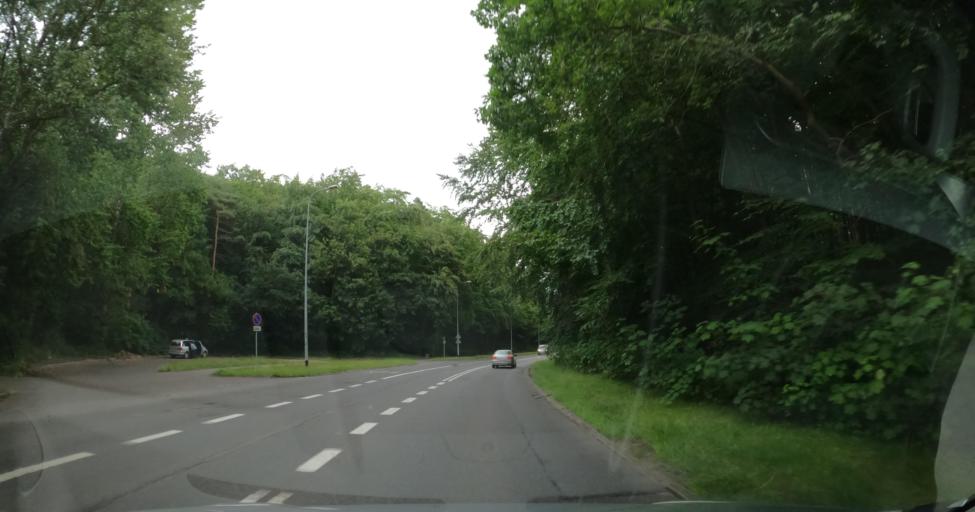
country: PL
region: Pomeranian Voivodeship
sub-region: Gdynia
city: Gdynia
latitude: 54.4955
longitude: 18.5209
